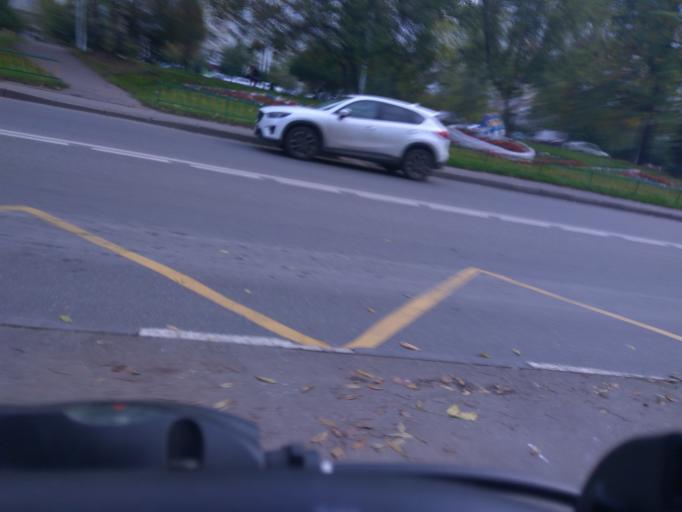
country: RU
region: Moskovskaya
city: Vostochnoe Degunino
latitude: 55.8808
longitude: 37.5641
